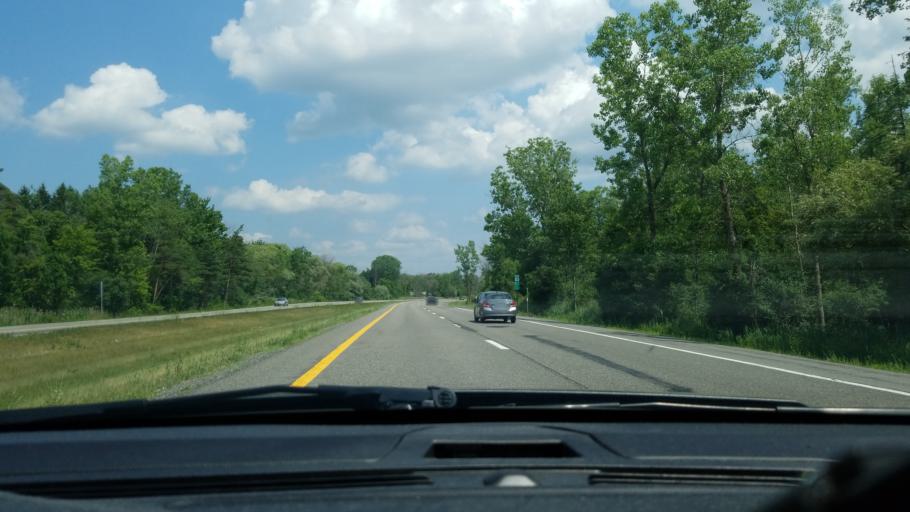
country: US
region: New York
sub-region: Onondaga County
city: North Syracuse
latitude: 43.1575
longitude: -76.1529
